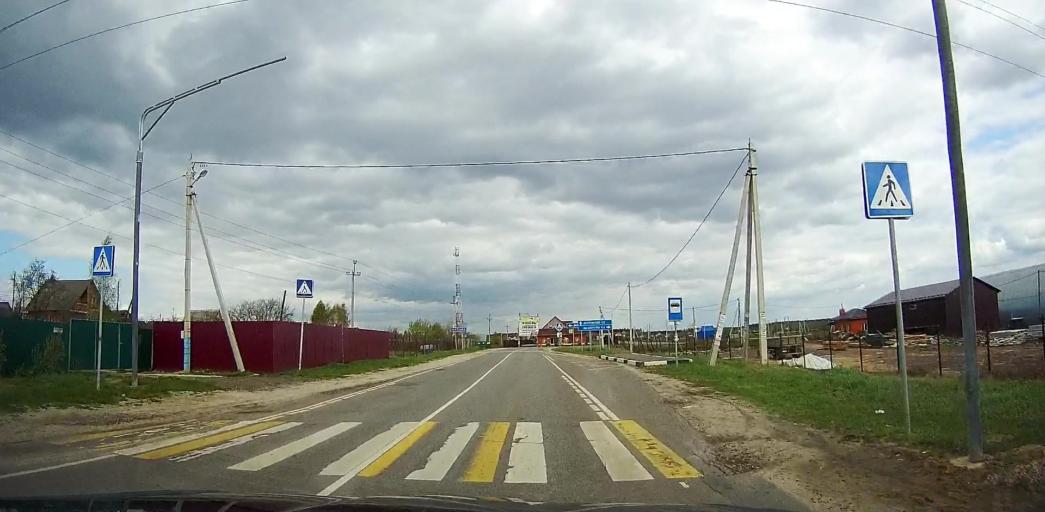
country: RU
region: Moskovskaya
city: Imeni Tsyurupy
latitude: 55.4968
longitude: 38.6224
